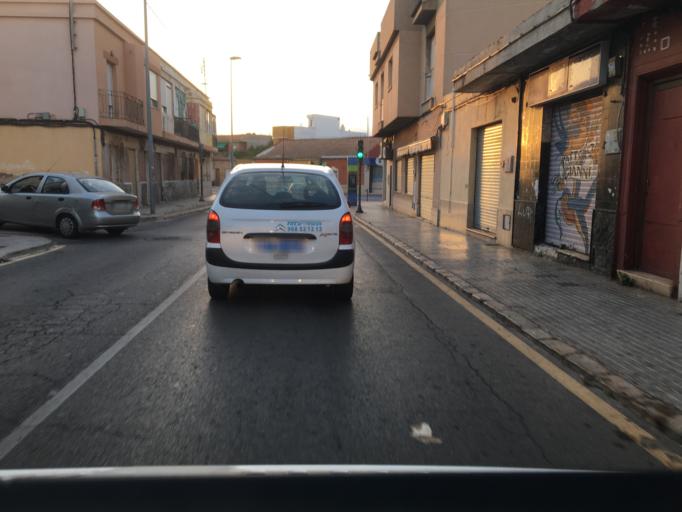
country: ES
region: Murcia
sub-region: Murcia
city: Cartagena
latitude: 37.6288
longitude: -0.9962
